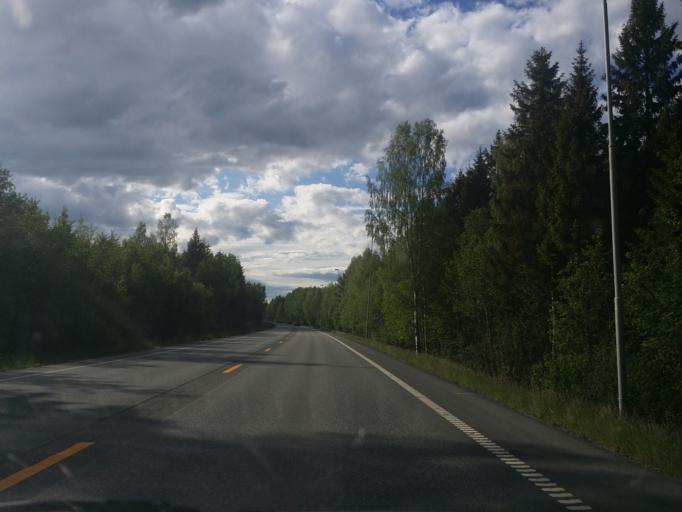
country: NO
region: Hedmark
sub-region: Stange
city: Stange
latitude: 60.7607
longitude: 11.1889
